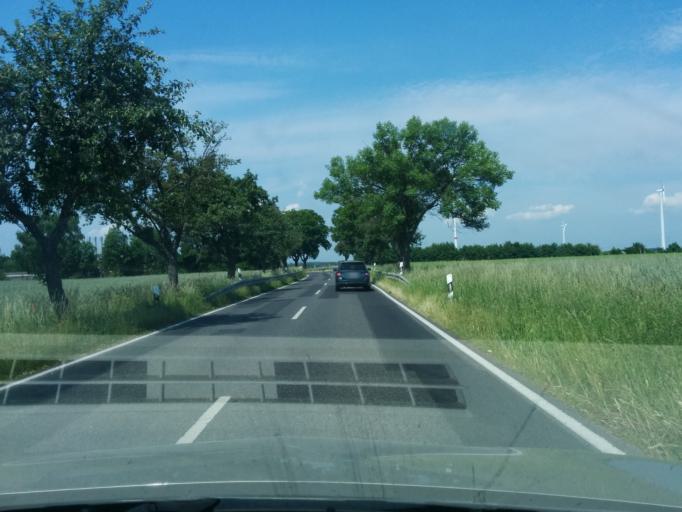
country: DE
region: Brandenburg
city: Ahrensfelde
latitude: 52.6105
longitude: 13.5973
